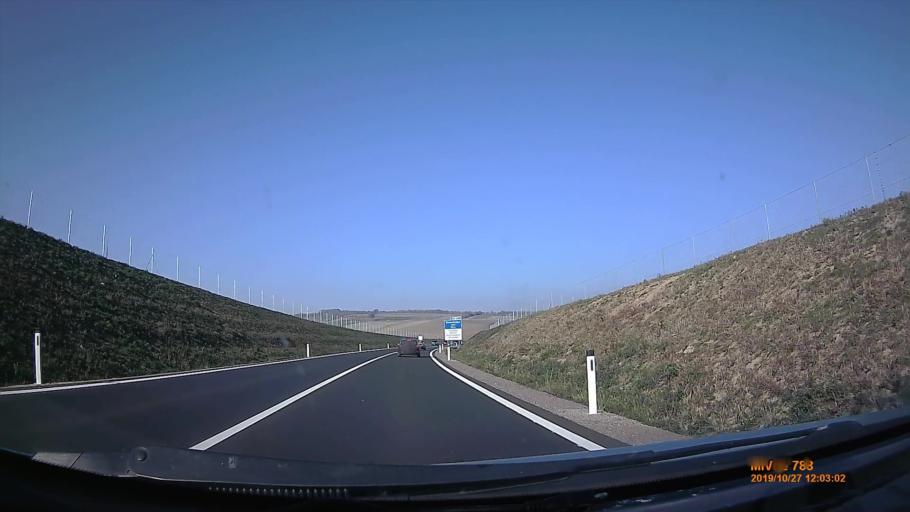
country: AT
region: Lower Austria
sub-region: Politischer Bezirk Mistelbach
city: Drasenhofen
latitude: 48.7387
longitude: 16.6412
